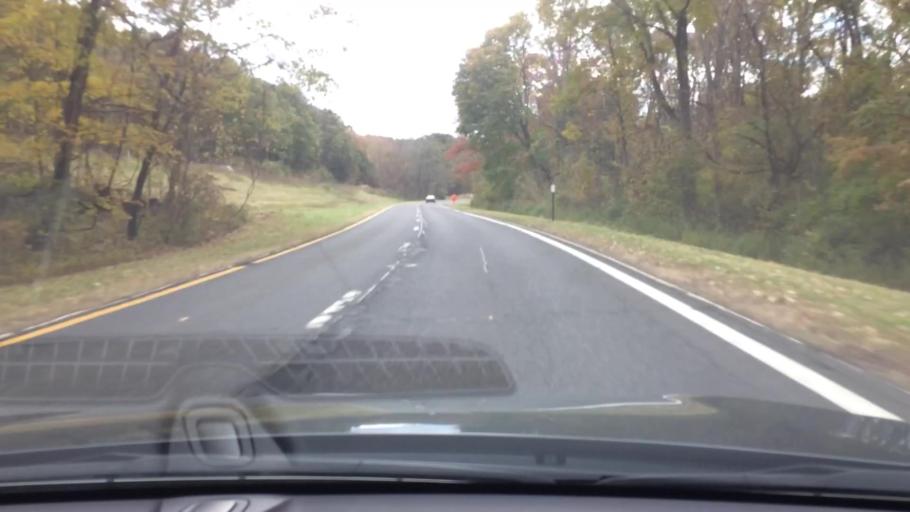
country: US
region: New York
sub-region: Dutchess County
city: Pleasant Valley
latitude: 41.7331
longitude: -73.7792
